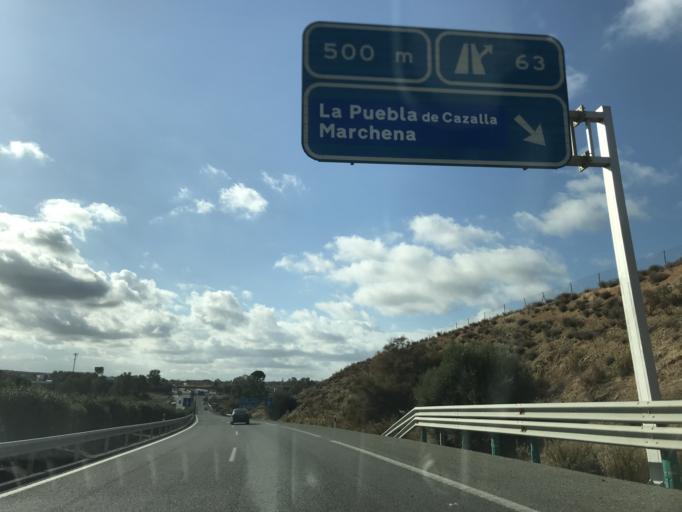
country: ES
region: Andalusia
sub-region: Provincia de Sevilla
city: La Puebla de Cazalla
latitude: 37.2340
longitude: -5.3143
